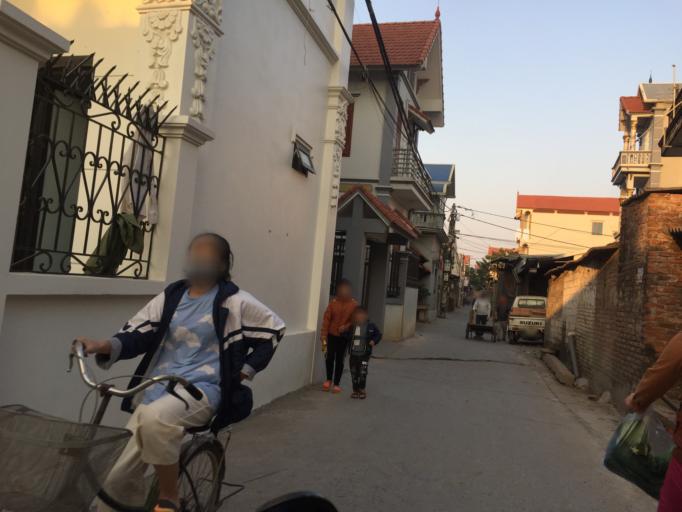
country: VN
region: Ha Noi
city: Chuc Son
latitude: 20.9087
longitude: 105.7283
